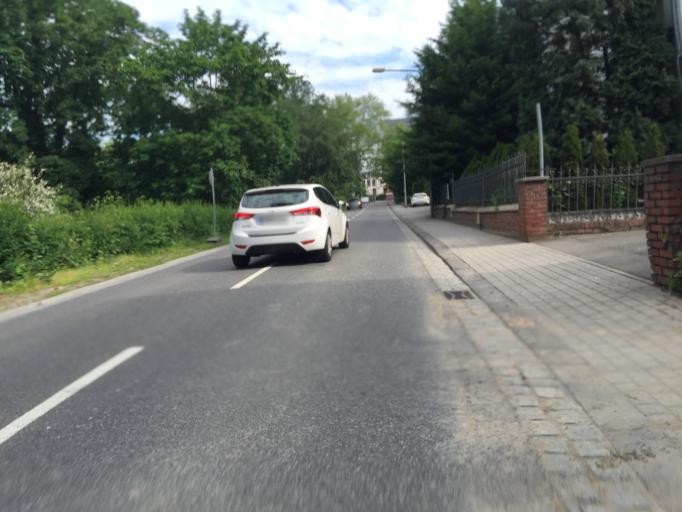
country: DE
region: Hesse
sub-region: Regierungsbezirk Darmstadt
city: Wiesbaden
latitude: 50.0890
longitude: 8.2601
